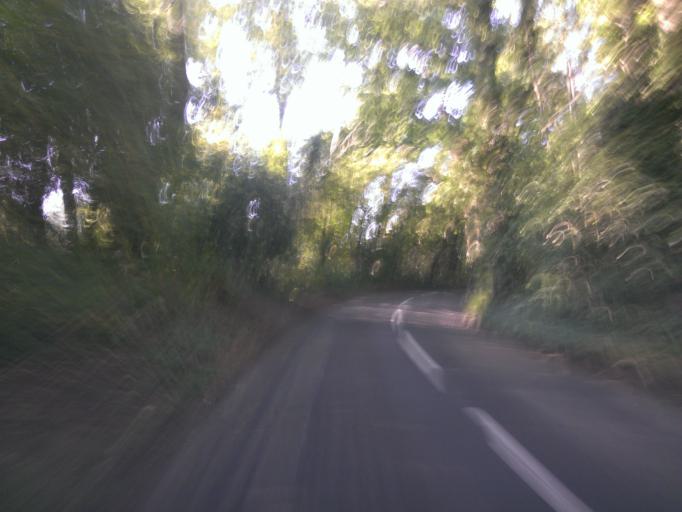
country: GB
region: England
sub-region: Kent
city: Edenbridge
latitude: 51.1928
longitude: 0.1093
